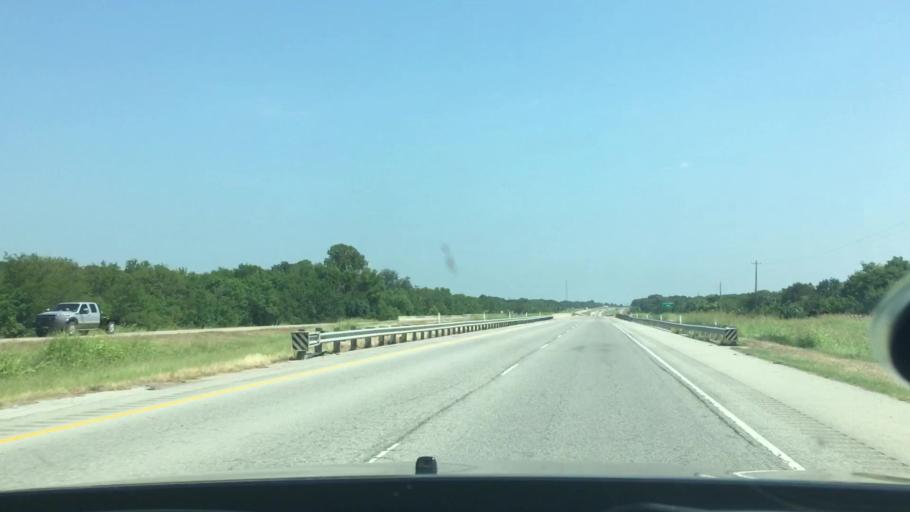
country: US
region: Oklahoma
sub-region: Atoka County
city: Atoka
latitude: 34.2535
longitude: -96.2139
